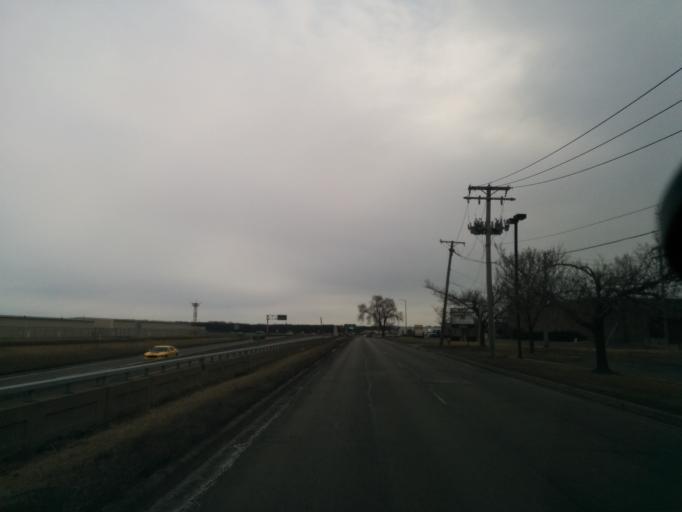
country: US
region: Illinois
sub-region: Cook County
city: Prospect Heights
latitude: 42.1094
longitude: -87.9058
